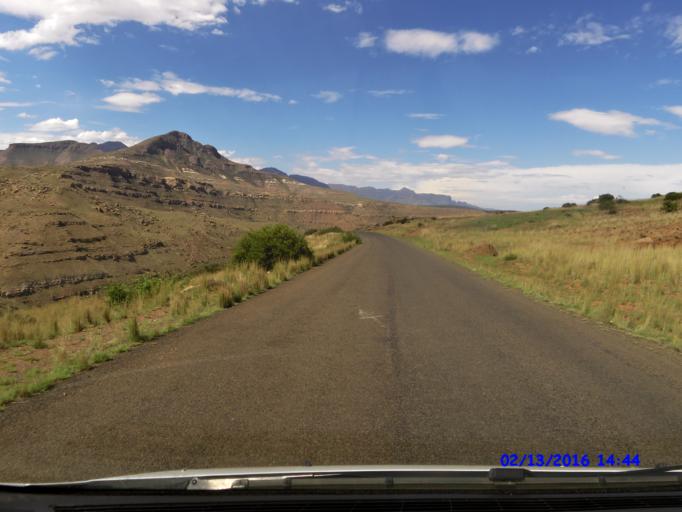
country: LS
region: Qacha's Nek
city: Qacha's Nek
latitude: -30.0678
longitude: 28.3882
